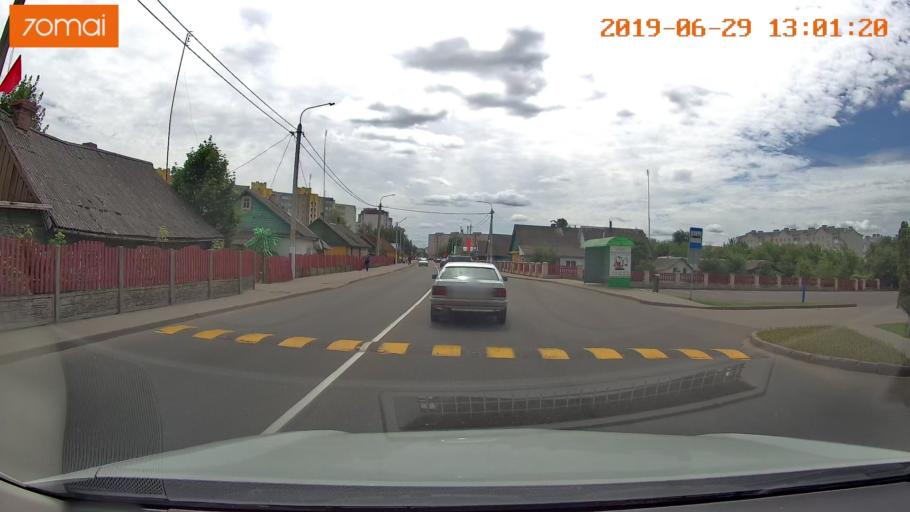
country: BY
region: Minsk
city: Slutsk
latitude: 53.0389
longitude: 27.5596
